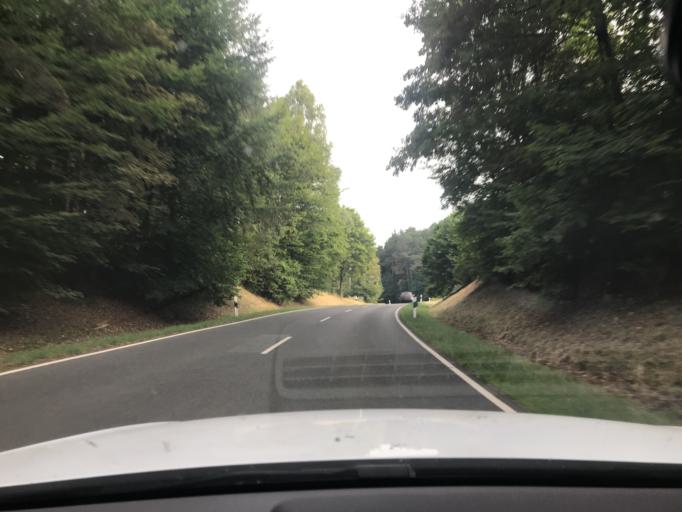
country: DE
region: Bavaria
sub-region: Upper Franconia
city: Pegnitz
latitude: 49.7573
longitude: 11.6052
